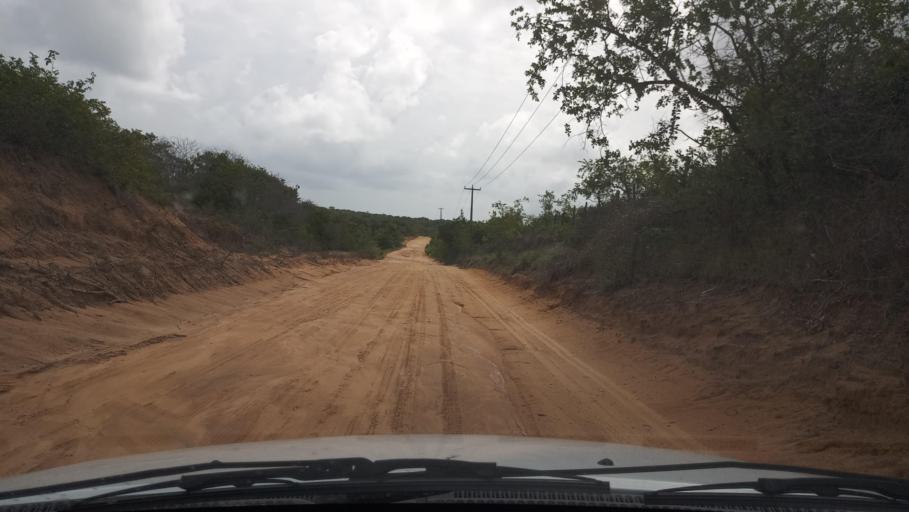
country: BR
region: Rio Grande do Norte
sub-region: Maxaranguape
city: Sao Miguel
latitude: -5.4837
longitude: -35.3070
